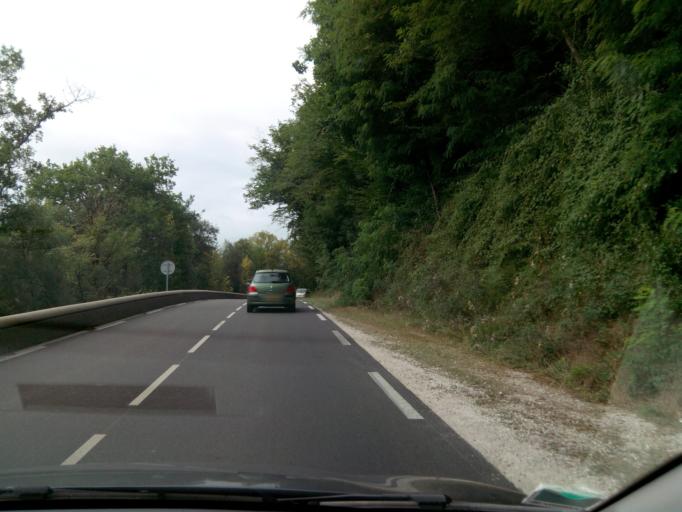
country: FR
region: Aquitaine
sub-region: Departement de la Dordogne
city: Eyvigues-et-Eybenes
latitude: 44.8604
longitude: 1.3486
